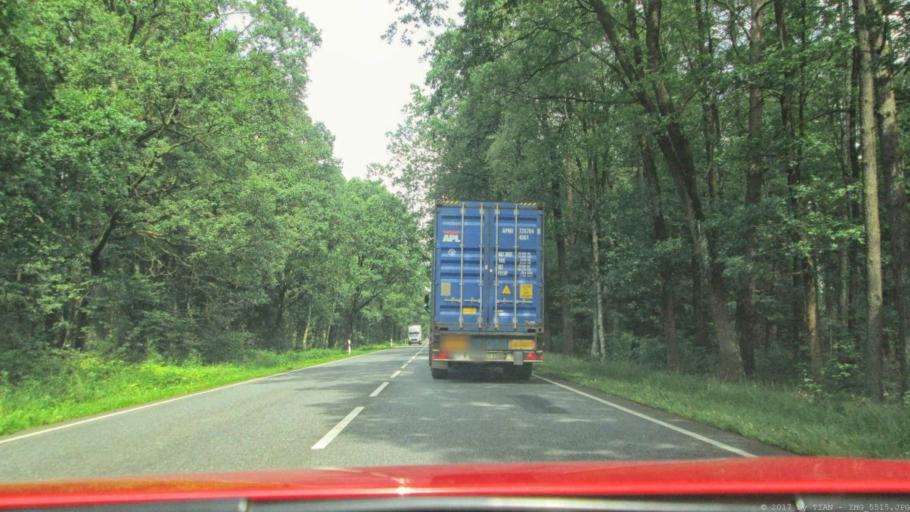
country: DE
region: Lower Saxony
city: Sprakensehl
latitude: 52.7851
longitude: 10.4910
